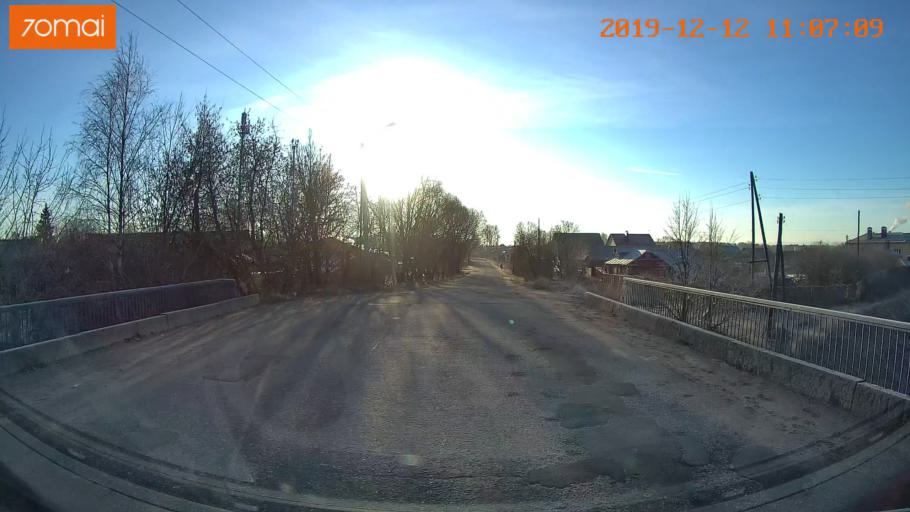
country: RU
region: Ivanovo
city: Kokhma
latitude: 56.9386
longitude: 41.0889
